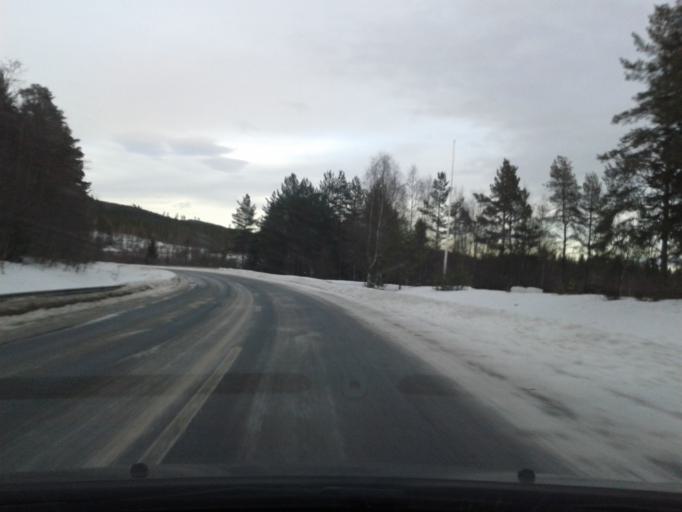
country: SE
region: Vaesternorrland
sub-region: Solleftea Kommun
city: Solleftea
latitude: 63.3325
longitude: 17.1250
